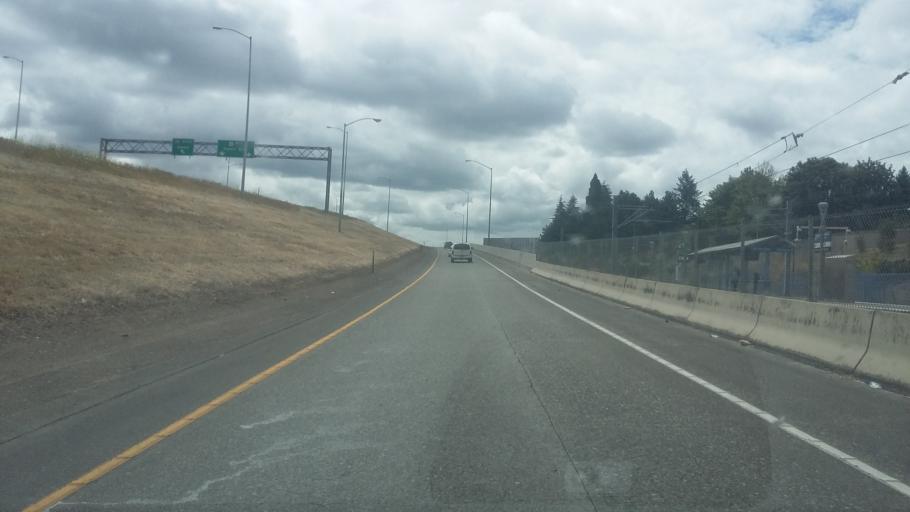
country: US
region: Oregon
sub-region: Multnomah County
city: Lents
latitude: 45.5038
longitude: -122.5664
